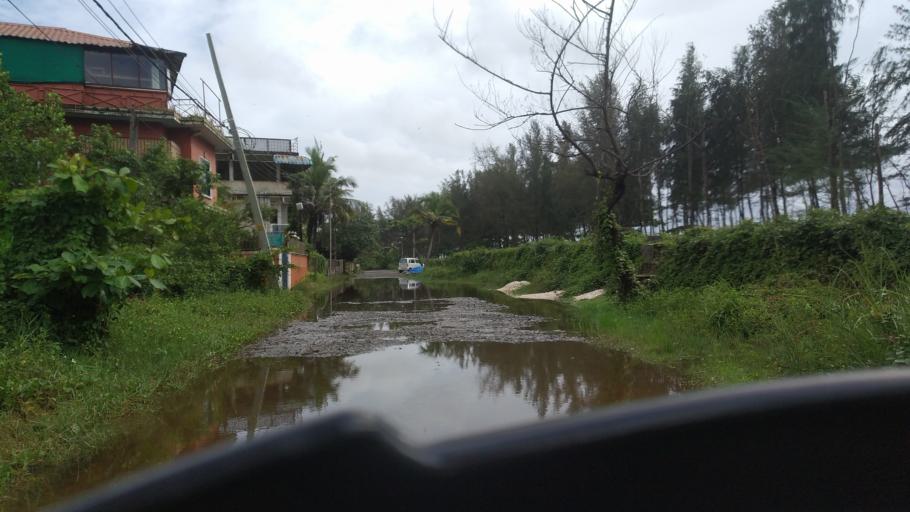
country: IN
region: Kerala
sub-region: Ernakulam
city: Elur
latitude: 10.1052
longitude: 76.1886
